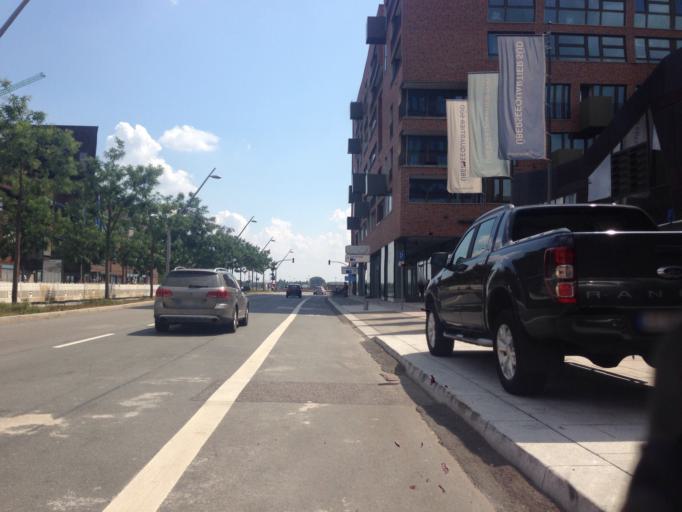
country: DE
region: Hamburg
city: Altstadt
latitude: 53.5424
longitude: 9.9988
